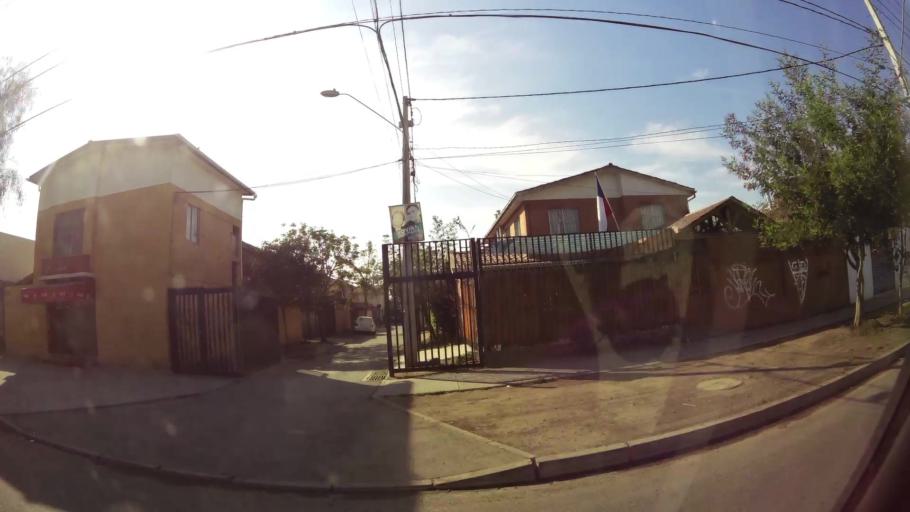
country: CL
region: Santiago Metropolitan
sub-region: Provincia de Santiago
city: Lo Prado
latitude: -33.4630
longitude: -70.7615
